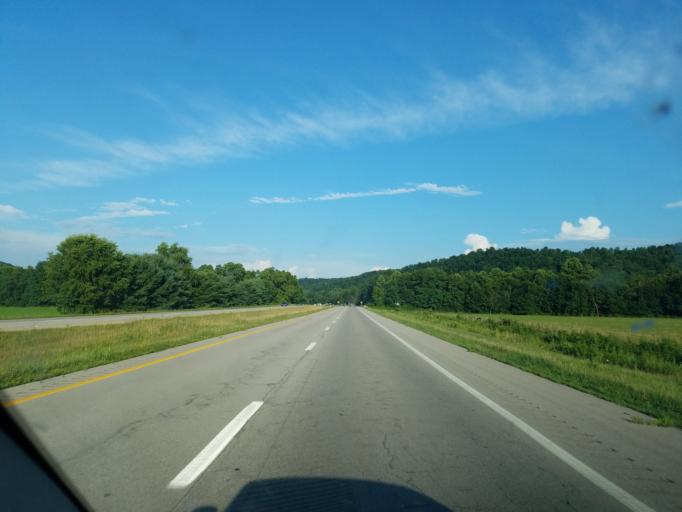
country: US
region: Ohio
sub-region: Pike County
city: Piketon
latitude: 39.0445
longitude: -83.1721
